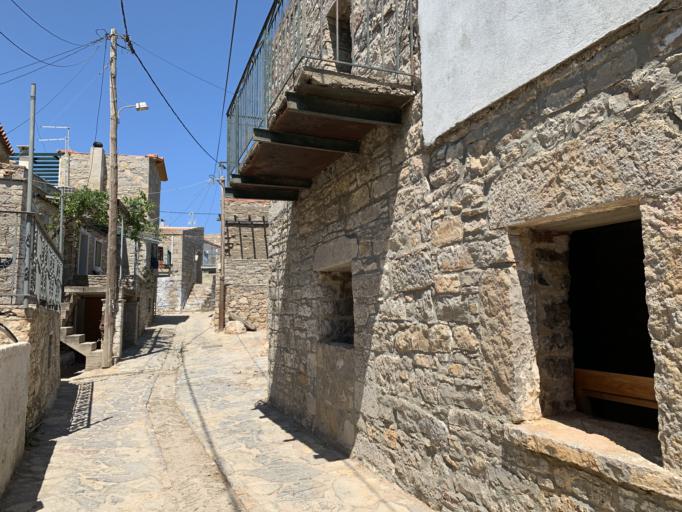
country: GR
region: North Aegean
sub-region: Chios
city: Vrontados
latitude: 38.4375
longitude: 25.9635
